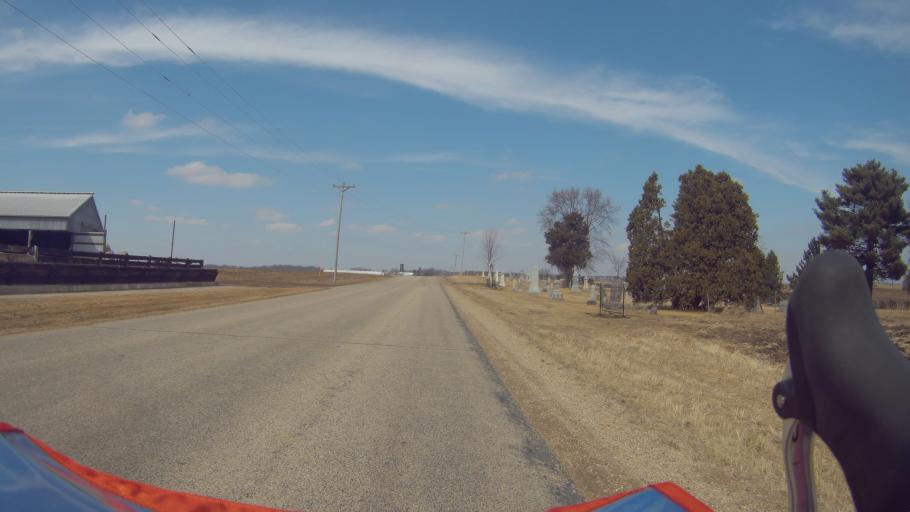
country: US
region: Wisconsin
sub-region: Dane County
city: Waunakee
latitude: 43.1699
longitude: -89.4966
